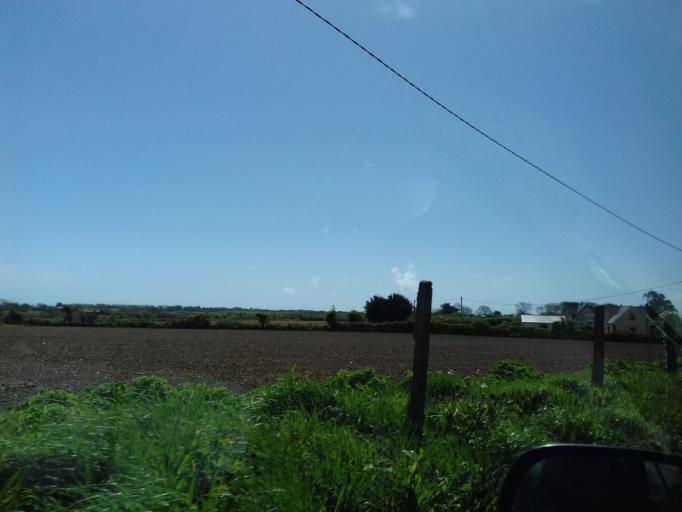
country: IE
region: Munster
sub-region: Waterford
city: Dunmore East
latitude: 52.1941
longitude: -6.8551
